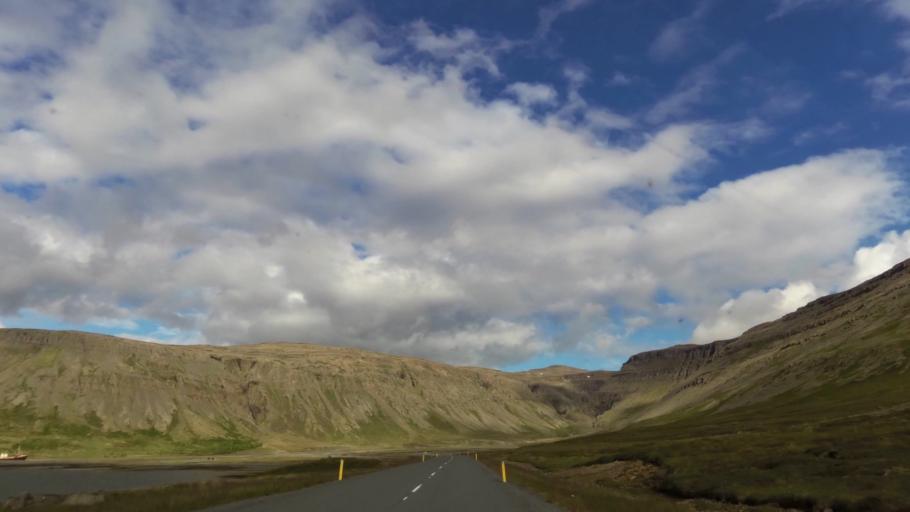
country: IS
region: West
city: Olafsvik
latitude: 65.5140
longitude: -23.8495
